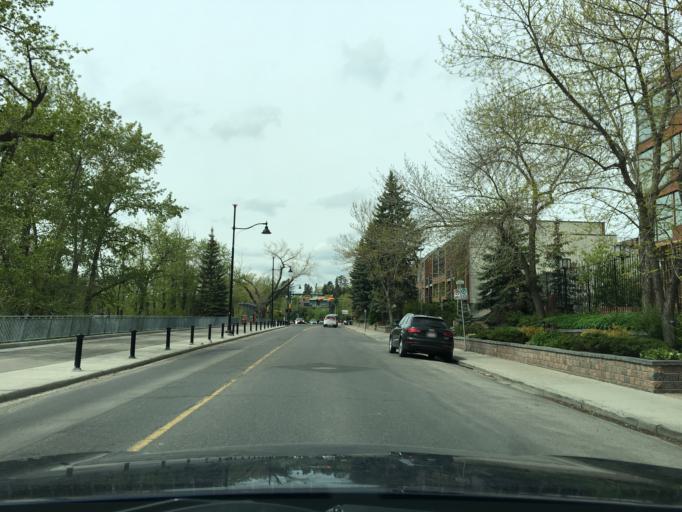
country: CA
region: Alberta
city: Calgary
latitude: 51.0296
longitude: -114.0688
